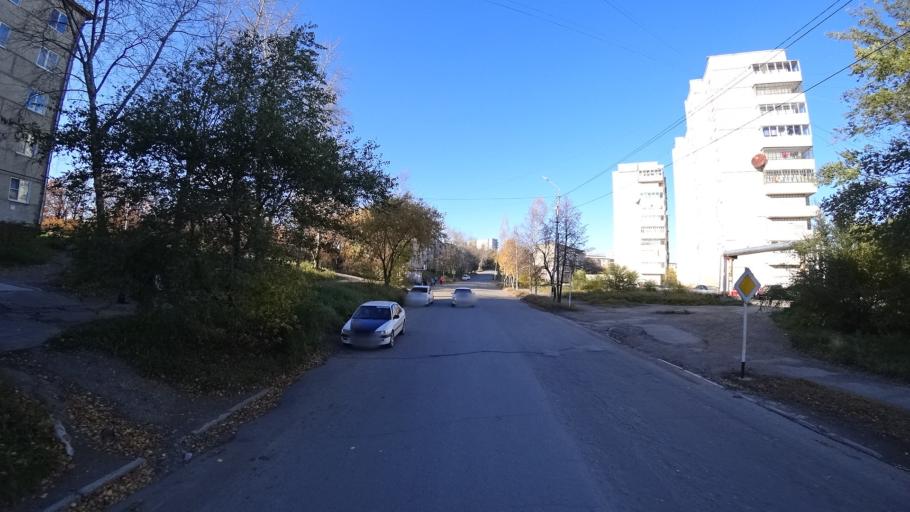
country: RU
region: Khabarovsk Krai
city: Amursk
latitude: 50.2374
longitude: 136.9050
